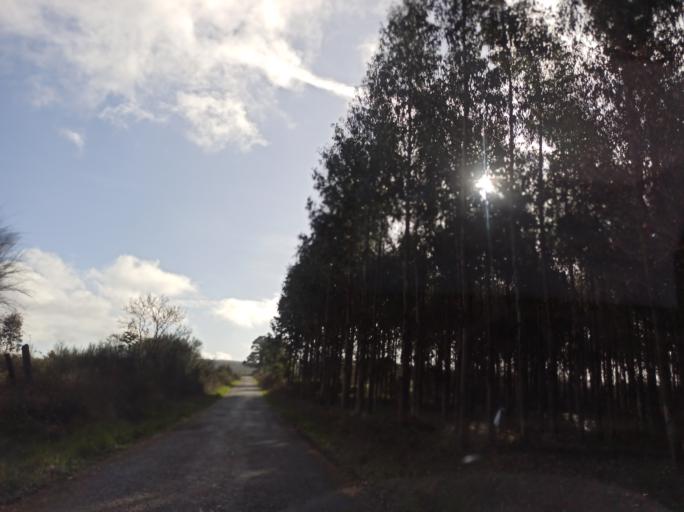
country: ES
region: Galicia
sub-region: Provincia da Coruna
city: Sobrado
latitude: 43.0809
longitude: -7.9583
